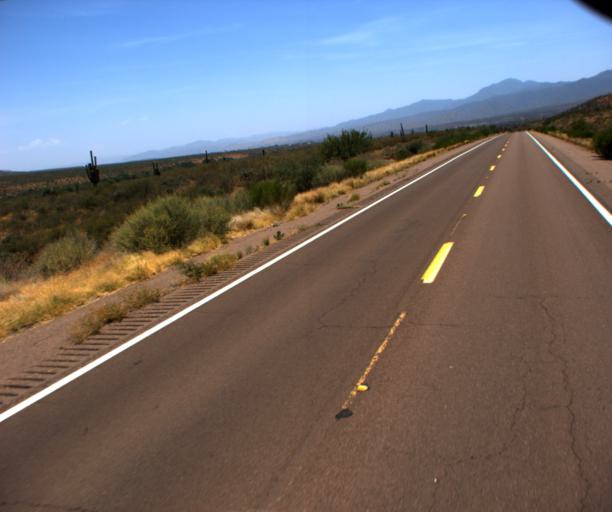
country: US
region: Arizona
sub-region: Gila County
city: Tonto Basin
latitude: 33.9055
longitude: -111.3103
